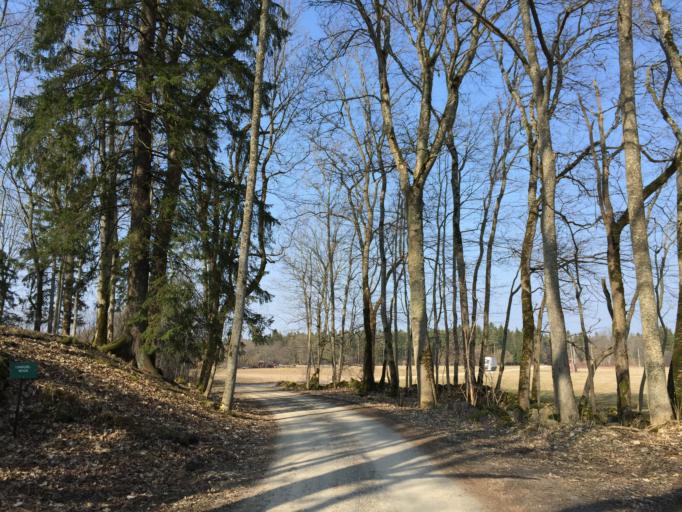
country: EE
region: Saare
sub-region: Kuressaare linn
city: Kuressaare
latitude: 58.3731
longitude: 22.6703
